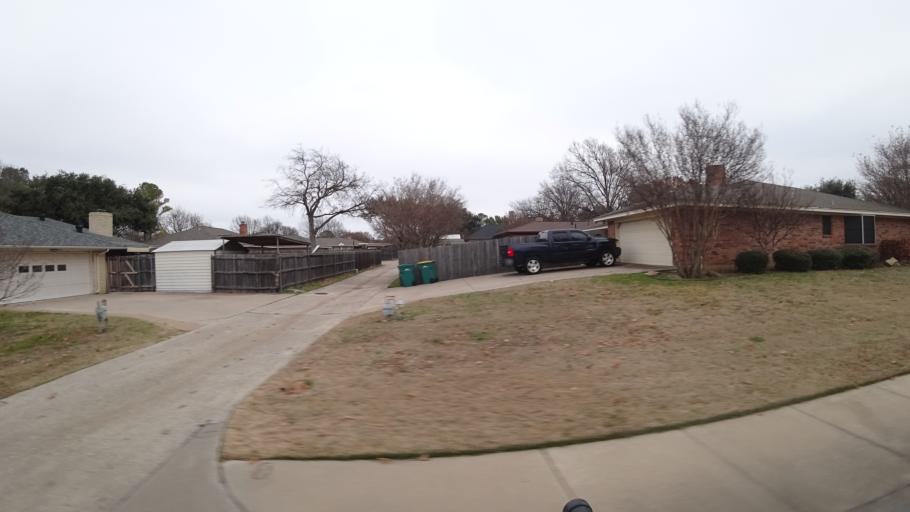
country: US
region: Texas
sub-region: Denton County
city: Lewisville
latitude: 33.0513
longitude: -97.0354
